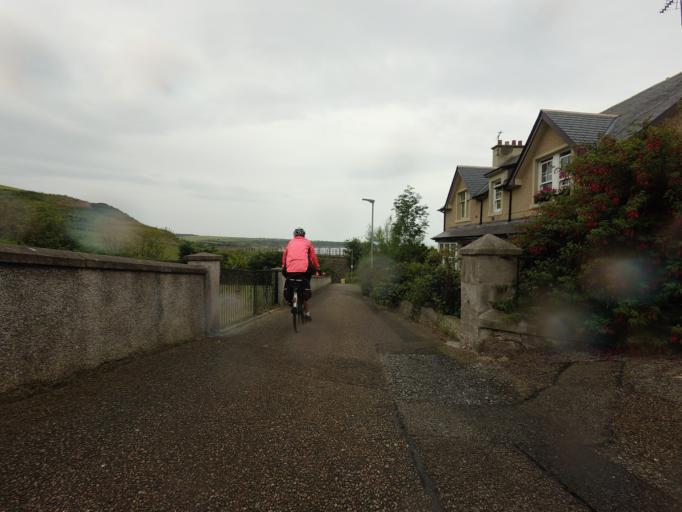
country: GB
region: Scotland
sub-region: Moray
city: Cullen
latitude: 57.6907
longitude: -2.8231
